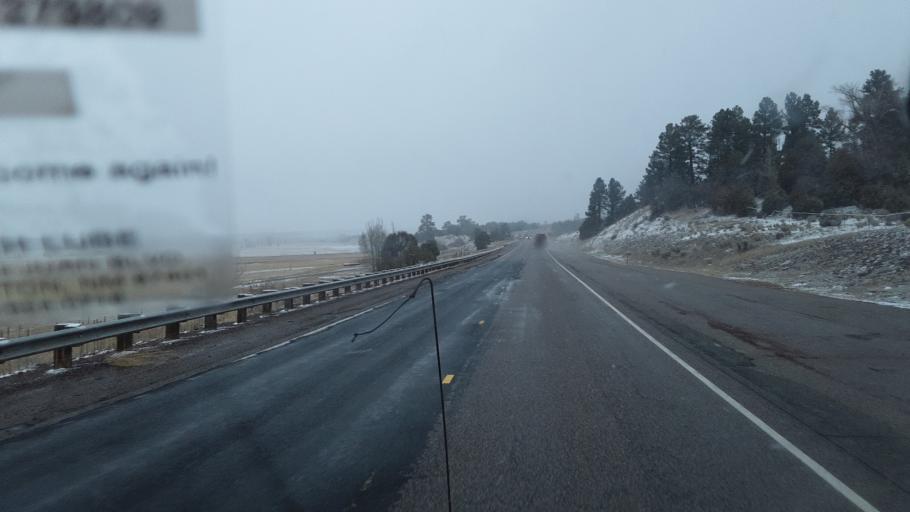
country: US
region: New Mexico
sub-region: Rio Arriba County
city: Tierra Amarilla
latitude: 36.7886
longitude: -106.5588
